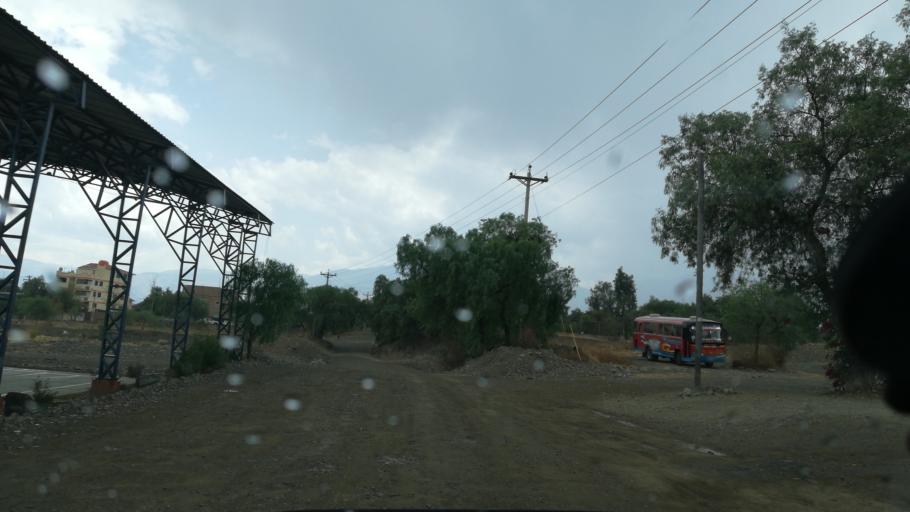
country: BO
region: Cochabamba
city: Cochabamba
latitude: -17.3386
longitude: -66.2124
